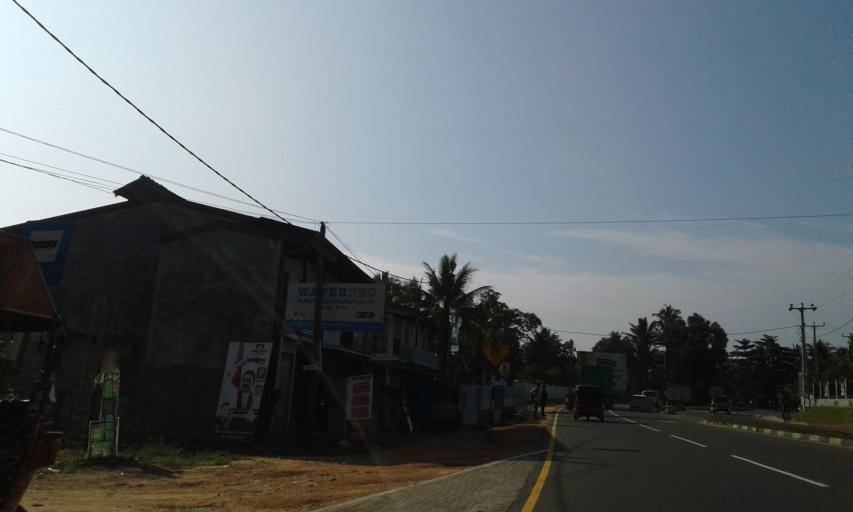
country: LK
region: Western
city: Gampaha
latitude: 7.0568
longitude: 80.0083
